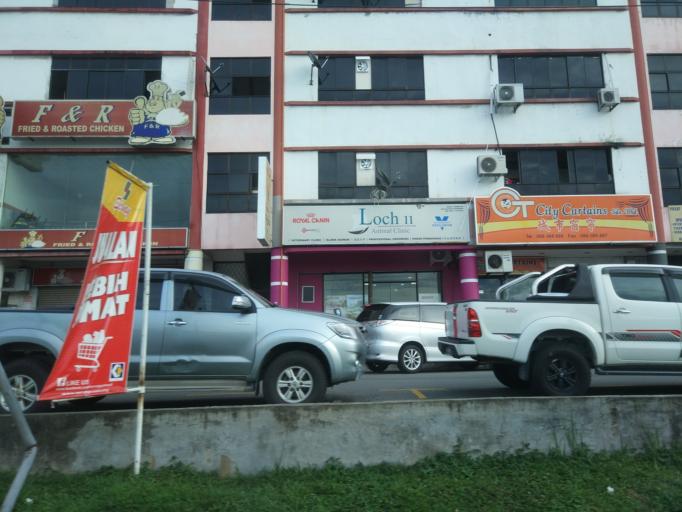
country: MY
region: Sabah
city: Kota Kinabalu
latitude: 5.9925
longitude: 116.1118
